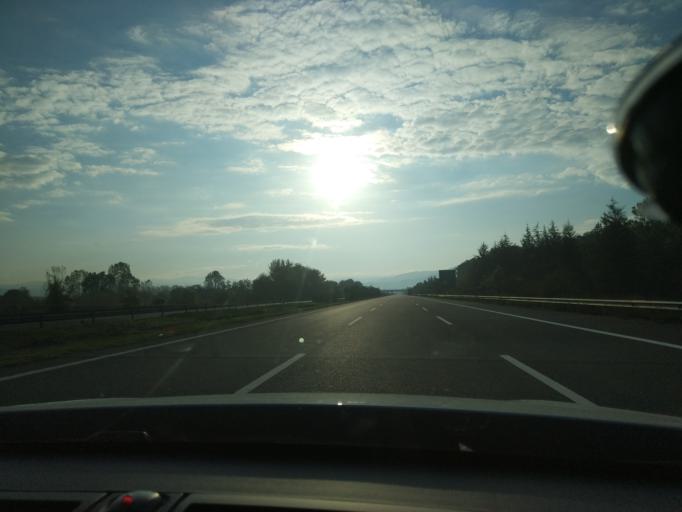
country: TR
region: Duzce
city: Duzce
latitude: 40.8016
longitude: 31.1781
